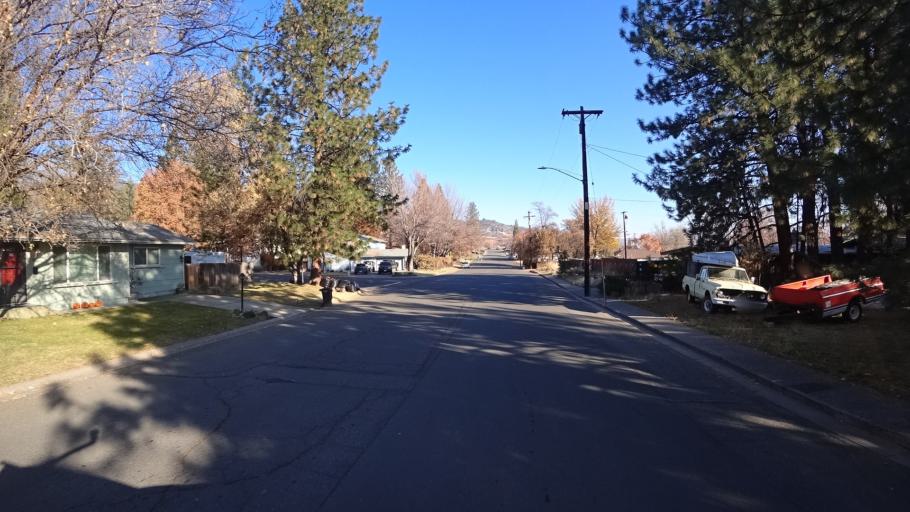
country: US
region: California
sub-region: Siskiyou County
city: Yreka
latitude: 41.7395
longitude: -122.6457
